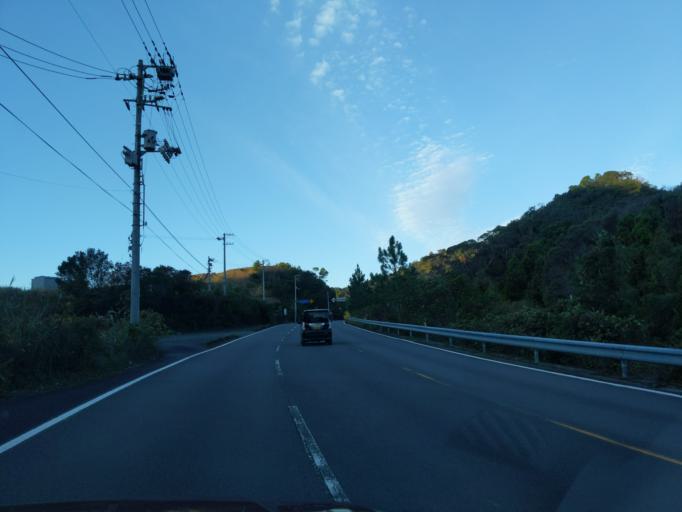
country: JP
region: Kochi
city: Muroto-misakicho
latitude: 33.6207
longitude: 134.3533
